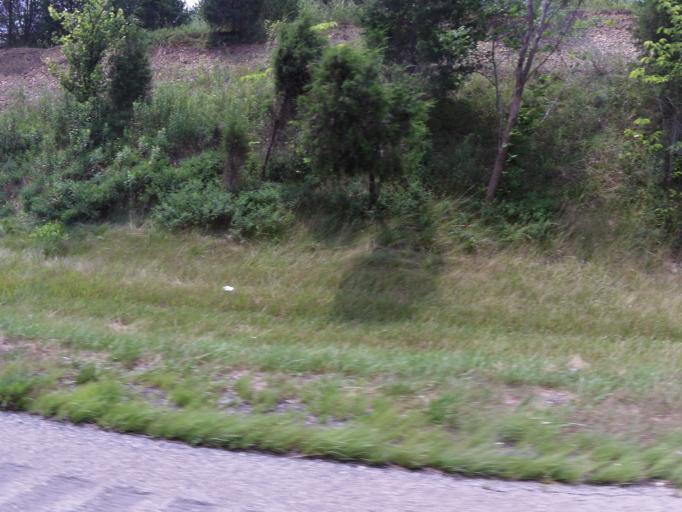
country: US
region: Kentucky
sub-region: Trimble County
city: Providence
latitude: 38.4783
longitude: -85.2700
